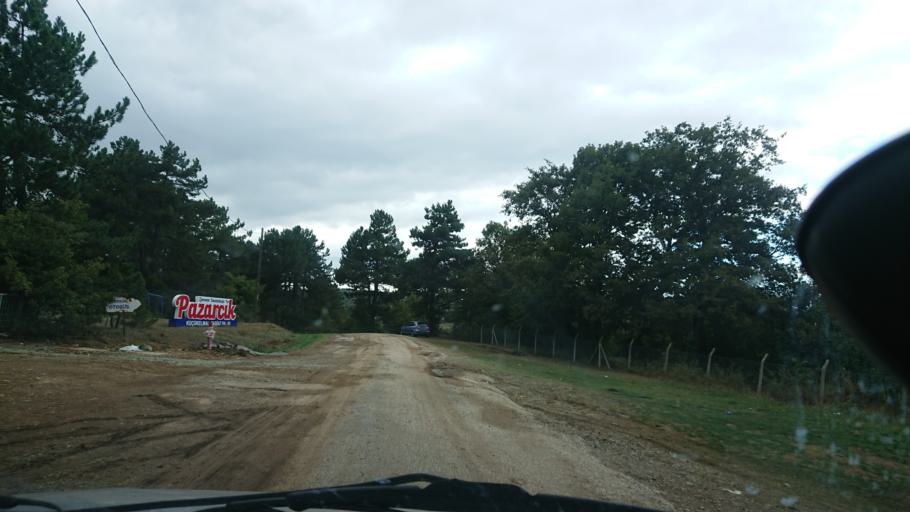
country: TR
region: Bilecik
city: Pazaryeri
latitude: 40.0132
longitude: 29.7976
